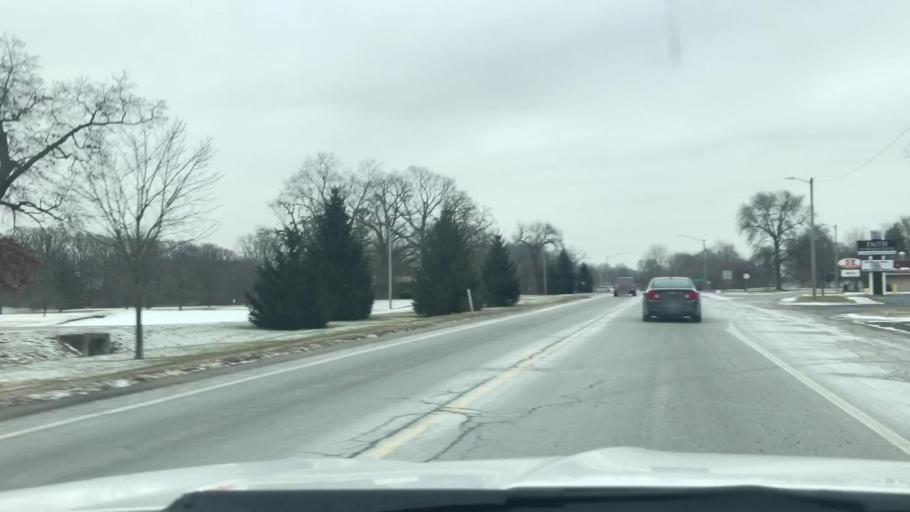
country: US
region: Indiana
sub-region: Fulton County
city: Rochester
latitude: 41.0628
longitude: -86.2014
